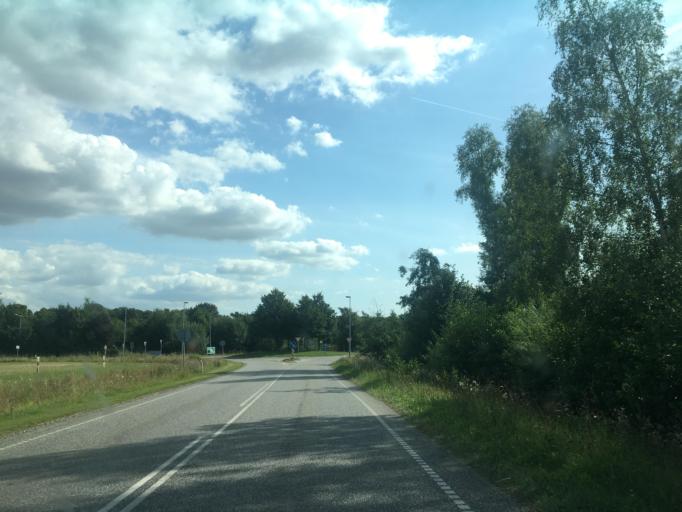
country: DK
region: South Denmark
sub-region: Middelfart Kommune
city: Ejby
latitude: 55.3936
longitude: 9.9637
